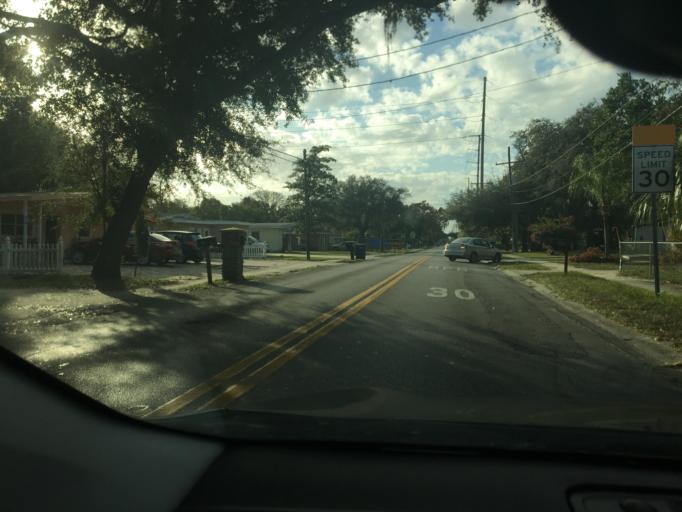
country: US
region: Florida
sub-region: Hillsborough County
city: University
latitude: 28.0436
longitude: -82.4349
